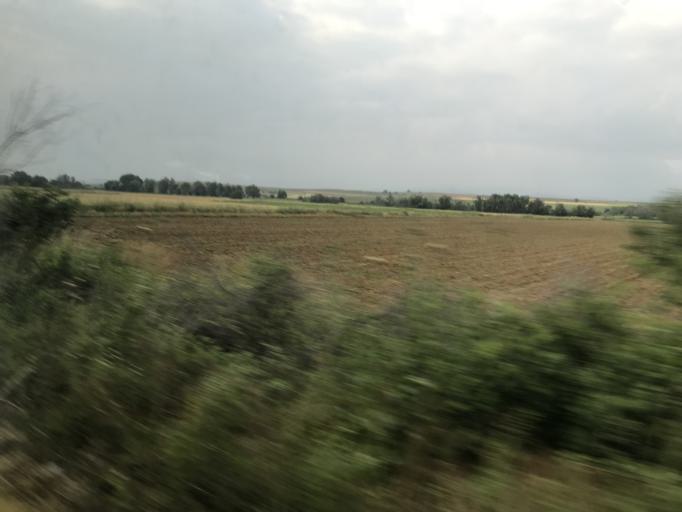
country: GR
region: East Macedonia and Thrace
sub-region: Nomos Rodopis
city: Lykeio
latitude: 41.0436
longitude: 25.6455
